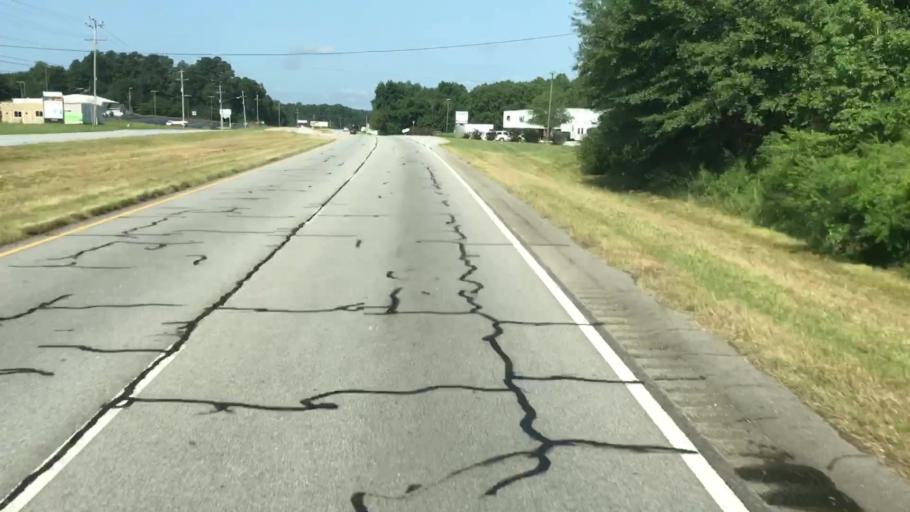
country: US
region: Georgia
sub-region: Walton County
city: Loganville
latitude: 33.8298
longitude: -83.8491
